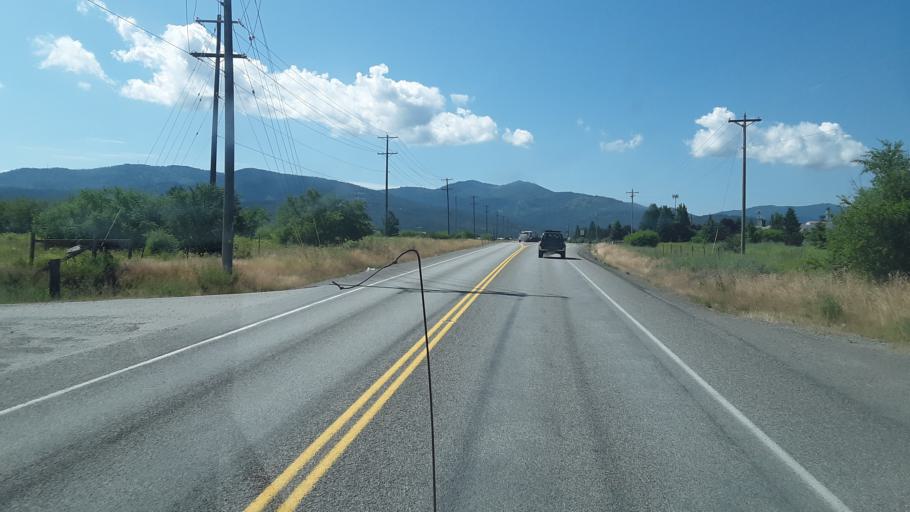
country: US
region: Idaho
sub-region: Kootenai County
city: Post Falls
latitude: 47.7237
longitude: -117.0017
